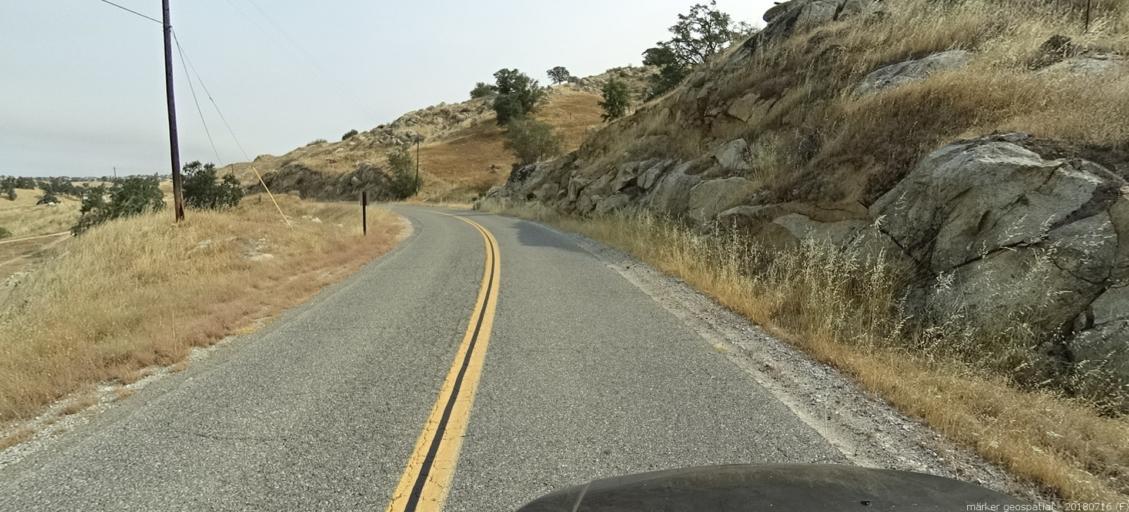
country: US
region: California
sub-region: Madera County
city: Bonadelle Ranchos-Madera Ranchos
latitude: 37.1078
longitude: -119.8668
